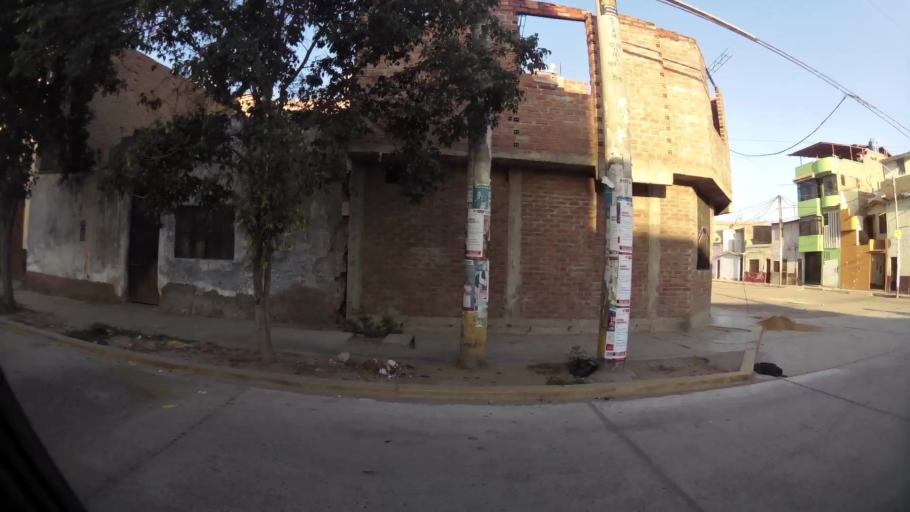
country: PE
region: Lambayeque
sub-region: Provincia de Chiclayo
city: Santa Rosa
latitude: -6.7720
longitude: -79.8295
